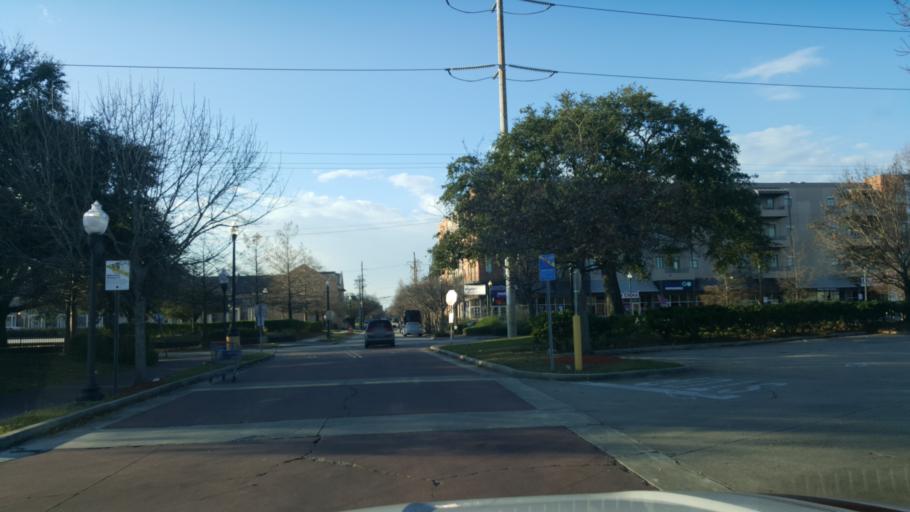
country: US
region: Louisiana
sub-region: Jefferson Parish
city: Gretna
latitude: 29.9268
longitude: -90.0689
